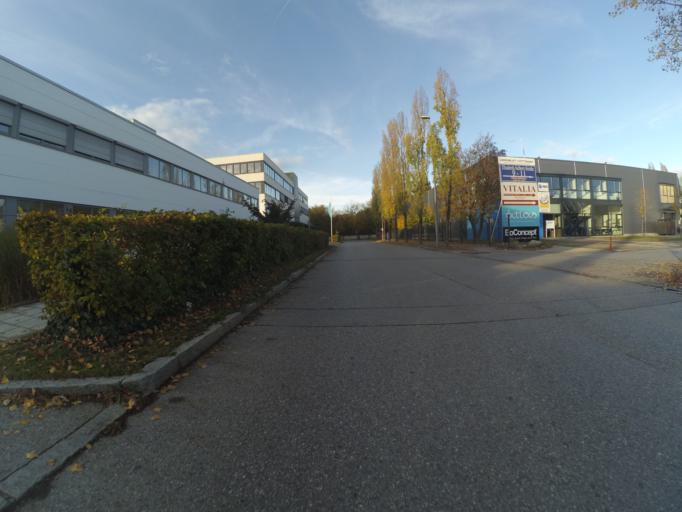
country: DE
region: Bavaria
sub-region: Upper Bavaria
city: Bogenhausen
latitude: 48.1958
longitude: 11.5901
